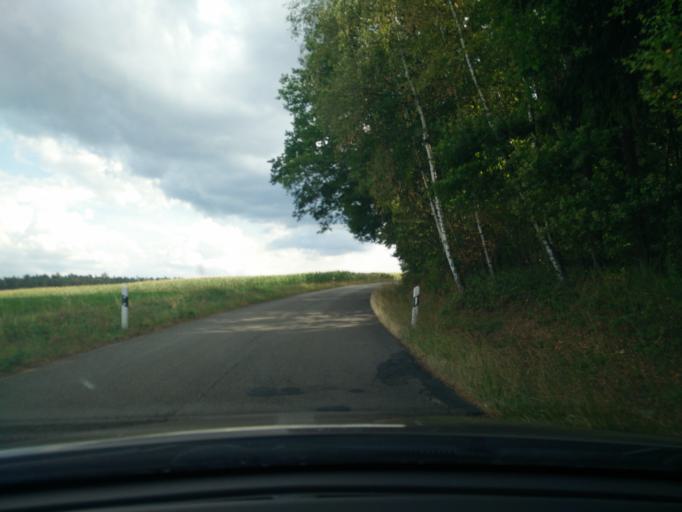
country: DE
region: Bavaria
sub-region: Regierungsbezirk Mittelfranken
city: Stein
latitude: 49.3844
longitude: 10.9845
